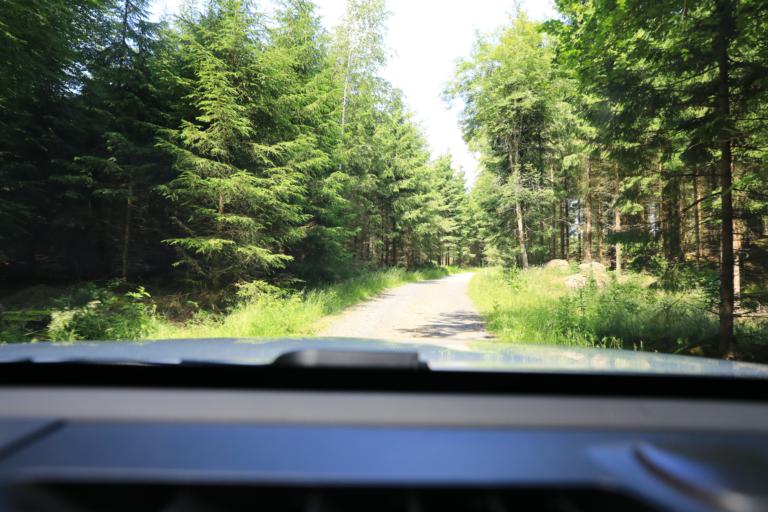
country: SE
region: Halland
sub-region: Varbergs Kommun
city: Tvaaker
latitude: 57.0932
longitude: 12.4930
